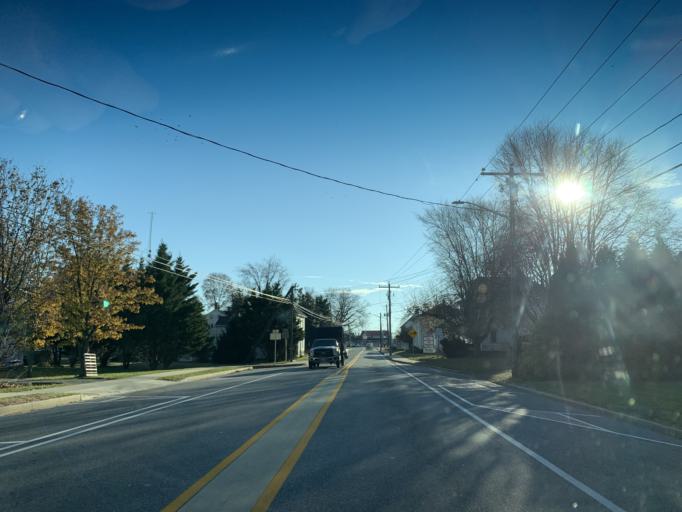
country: US
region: Delaware
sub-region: New Castle County
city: Middletown
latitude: 39.4064
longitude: -75.8667
